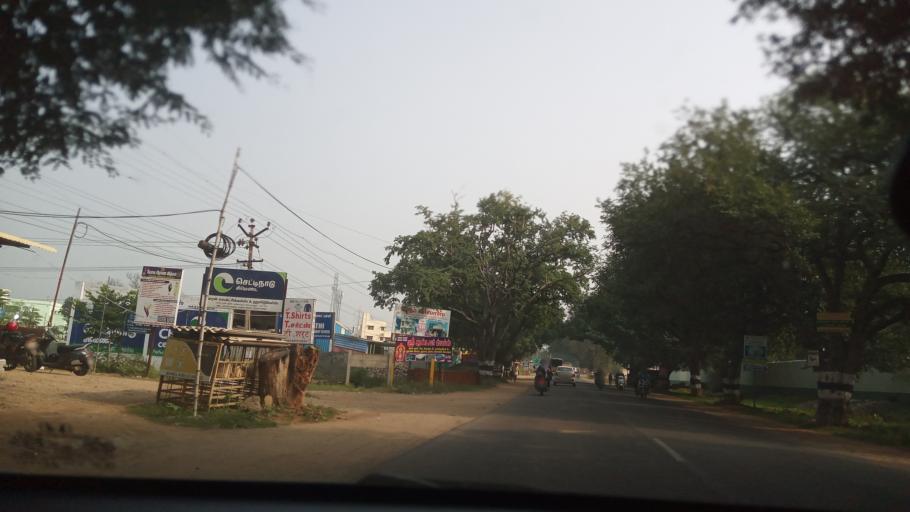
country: IN
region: Tamil Nadu
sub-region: Coimbatore
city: Annur
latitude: 11.1693
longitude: 77.0538
